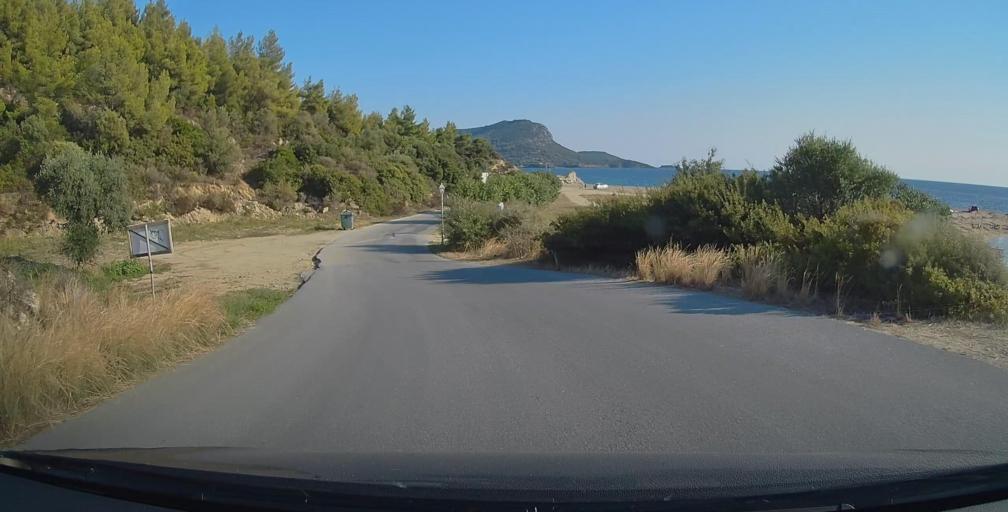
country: GR
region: Central Macedonia
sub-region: Nomos Chalkidikis
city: Sykia
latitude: 39.9926
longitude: 23.8932
